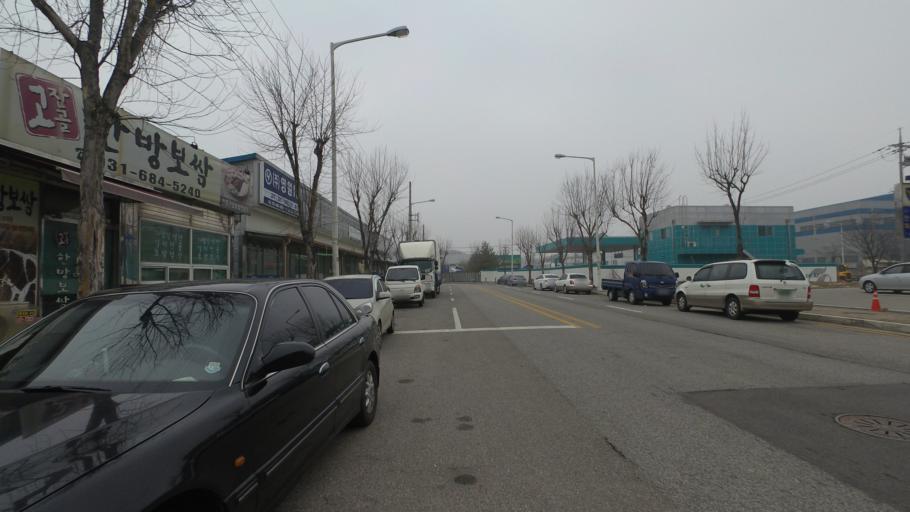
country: KR
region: Chungcheongnam-do
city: Tangjin
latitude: 36.9743
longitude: 126.8440
